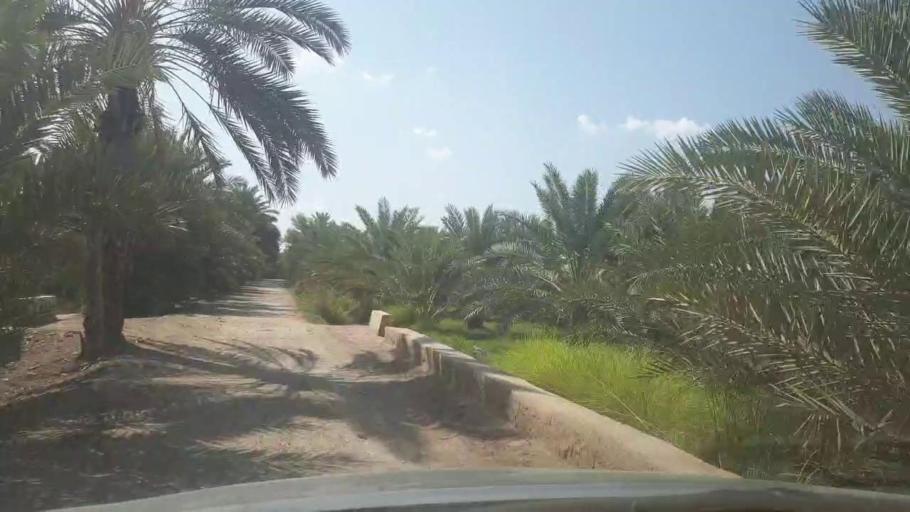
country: PK
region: Sindh
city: Khairpur
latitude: 27.5533
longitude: 68.8053
